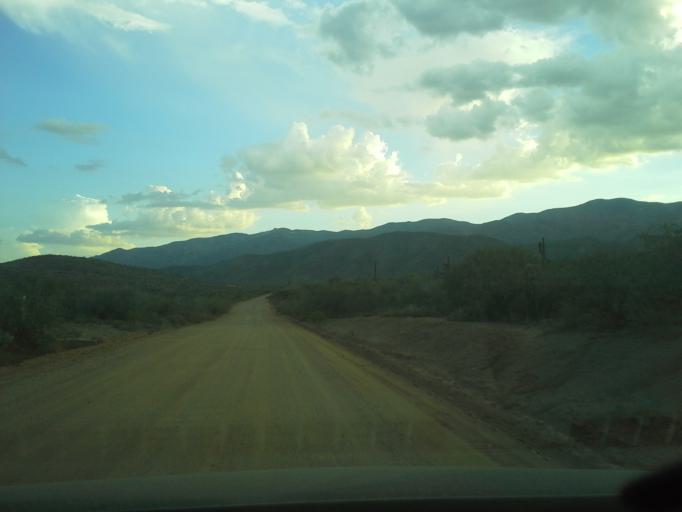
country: US
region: Arizona
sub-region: Yavapai County
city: Cordes Lakes
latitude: 34.1988
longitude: -112.1553
